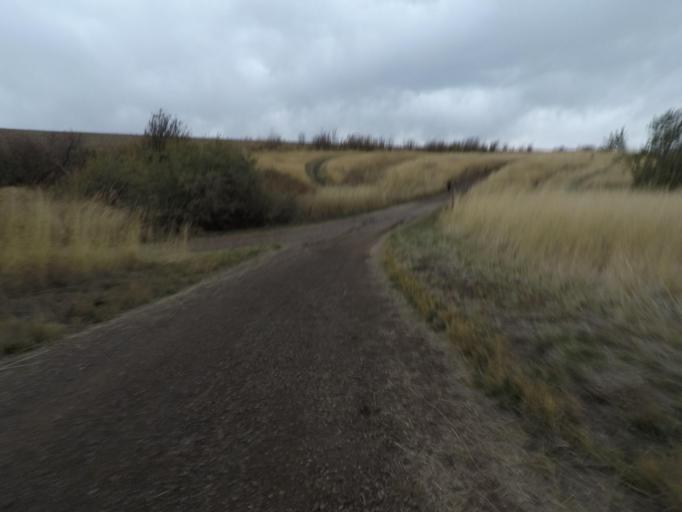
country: US
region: Washington
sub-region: Walla Walla County
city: Walla Walla East
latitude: 46.0599
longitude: -118.2573
